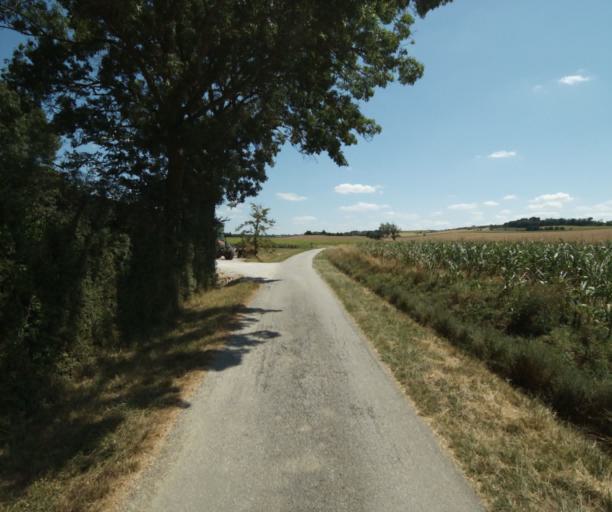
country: FR
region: Midi-Pyrenees
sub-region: Departement de la Haute-Garonne
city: Saint-Felix-Lauragais
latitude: 43.4847
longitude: 1.8757
